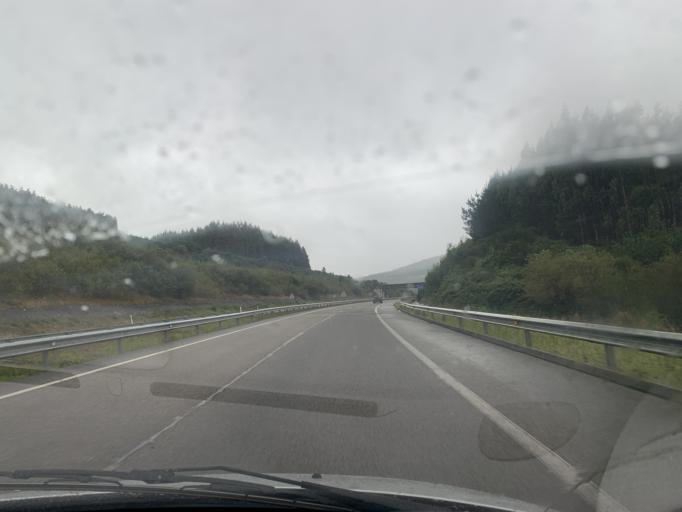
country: ES
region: Galicia
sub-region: Provincia de Lugo
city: Abadin
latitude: 43.3588
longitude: -7.4665
